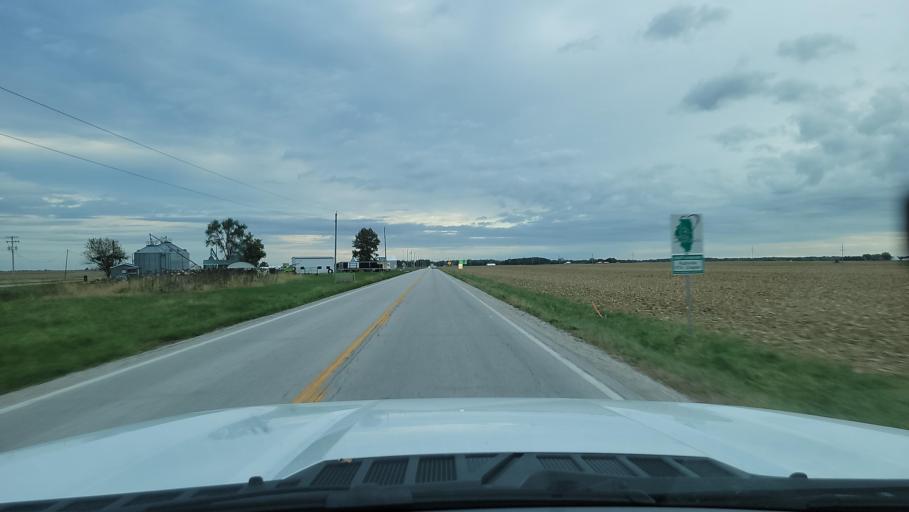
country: US
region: Illinois
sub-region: Schuyler County
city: Rushville
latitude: 40.1357
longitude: -90.5619
